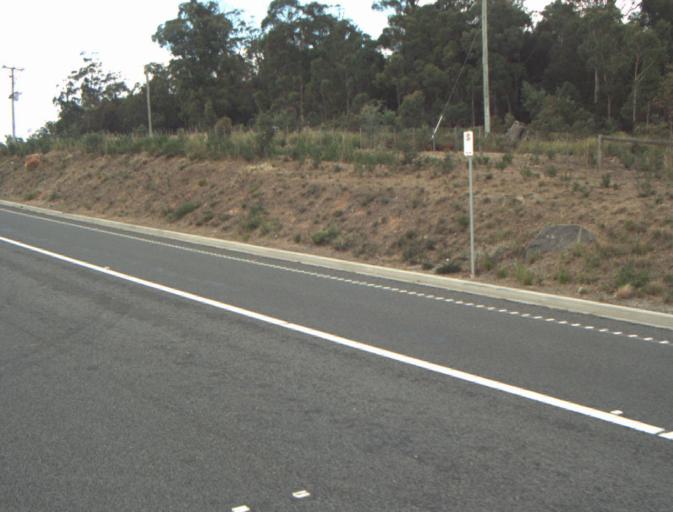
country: AU
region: Tasmania
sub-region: Launceston
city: Mayfield
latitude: -41.2658
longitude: 147.0330
